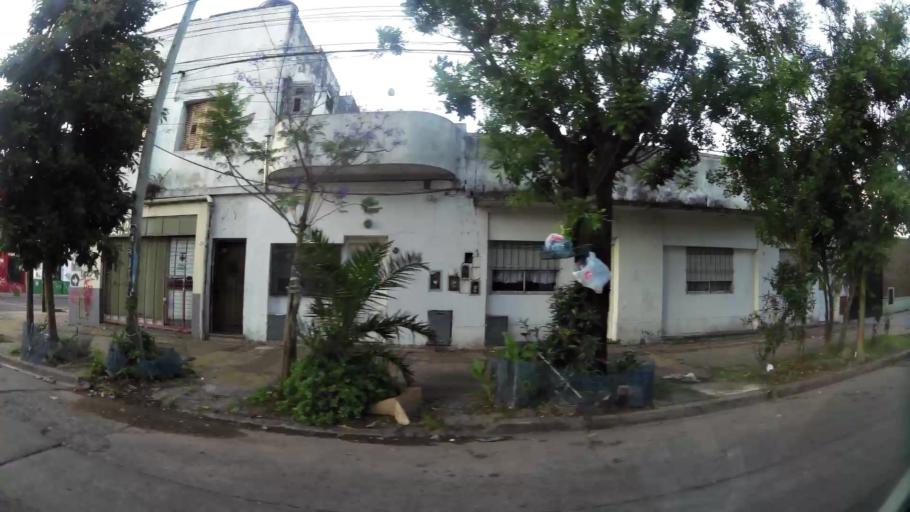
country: AR
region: Buenos Aires
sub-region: Partido de Moron
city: Moron
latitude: -34.6548
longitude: -58.6196
